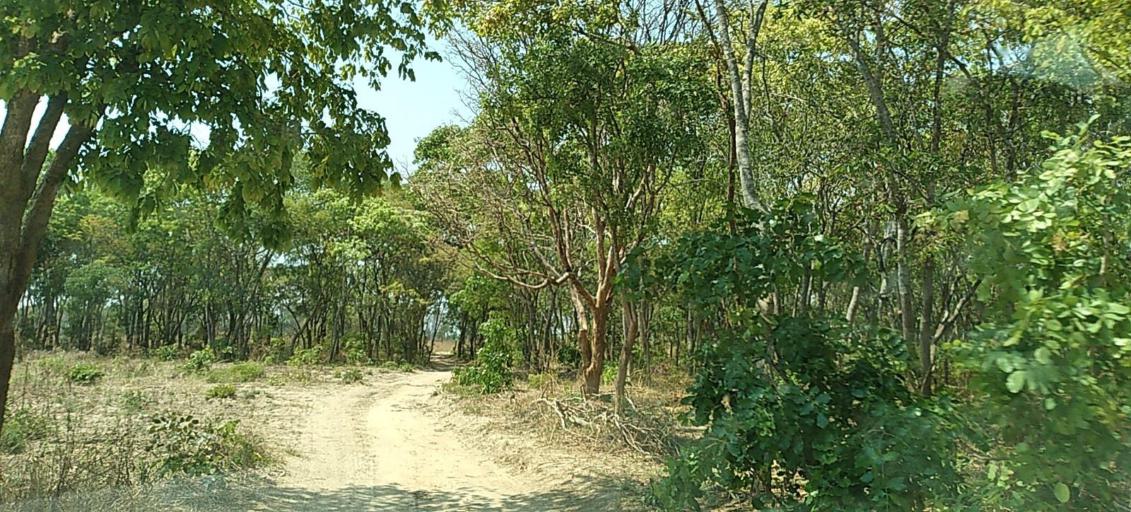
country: ZM
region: Copperbelt
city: Mpongwe
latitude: -13.8664
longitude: 28.0538
